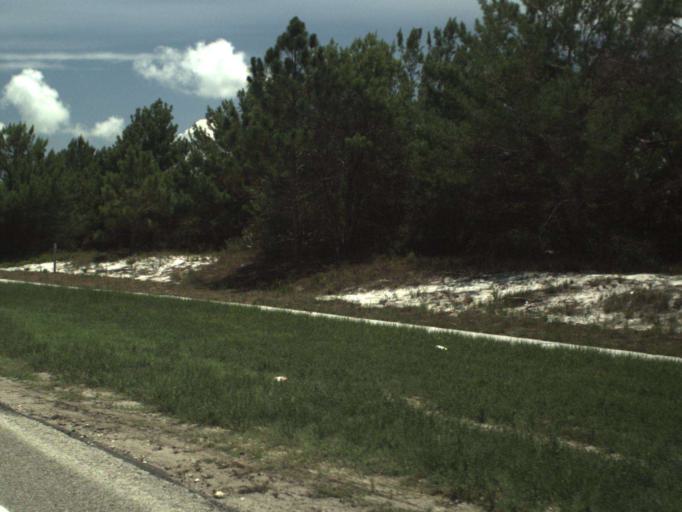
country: US
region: Florida
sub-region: Indian River County
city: Florida Ridge
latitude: 27.5524
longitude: -80.3700
